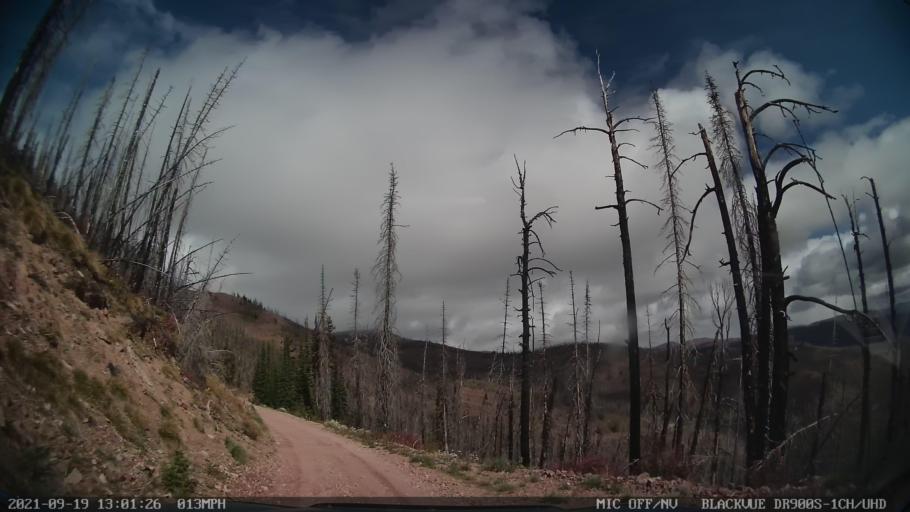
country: US
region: Montana
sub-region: Missoula County
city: Seeley Lake
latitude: 47.1854
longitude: -113.3545
